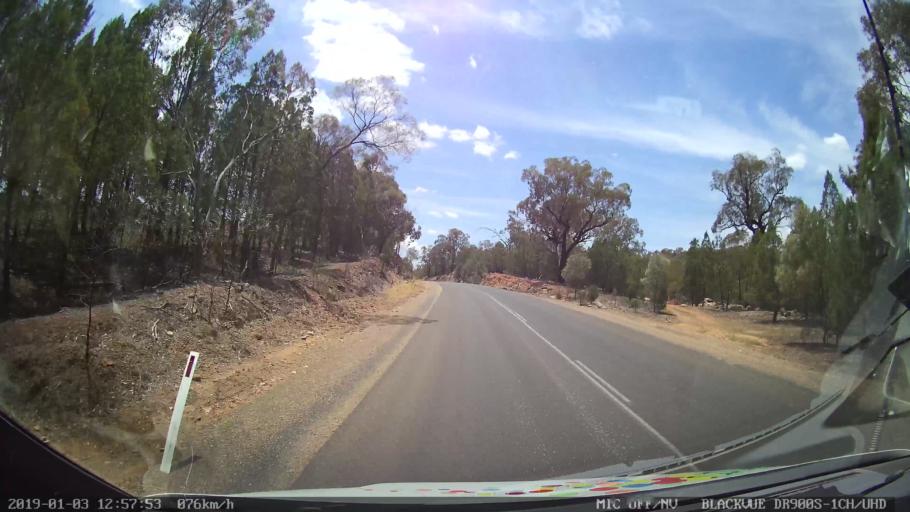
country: AU
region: New South Wales
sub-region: Cabonne
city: Canowindra
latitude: -33.6459
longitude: 148.3679
